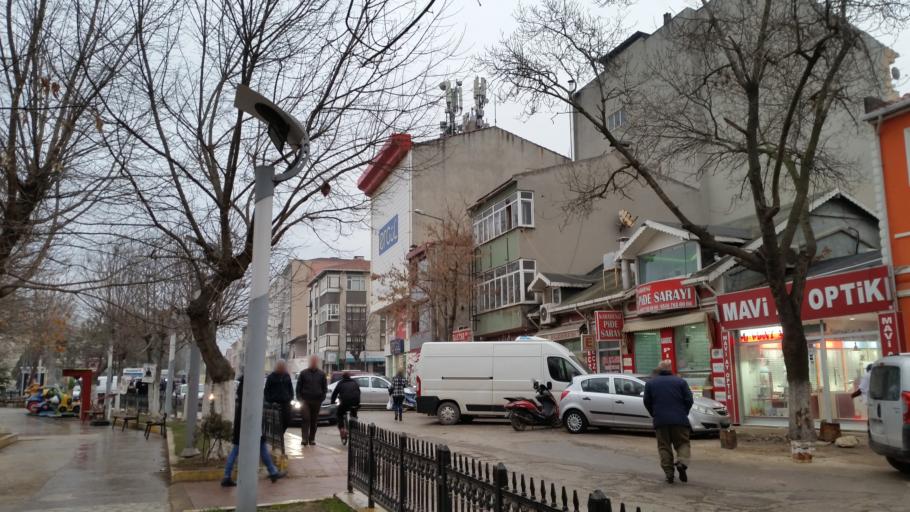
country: TR
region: Tekirdag
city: Saray
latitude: 41.4417
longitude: 27.9199
